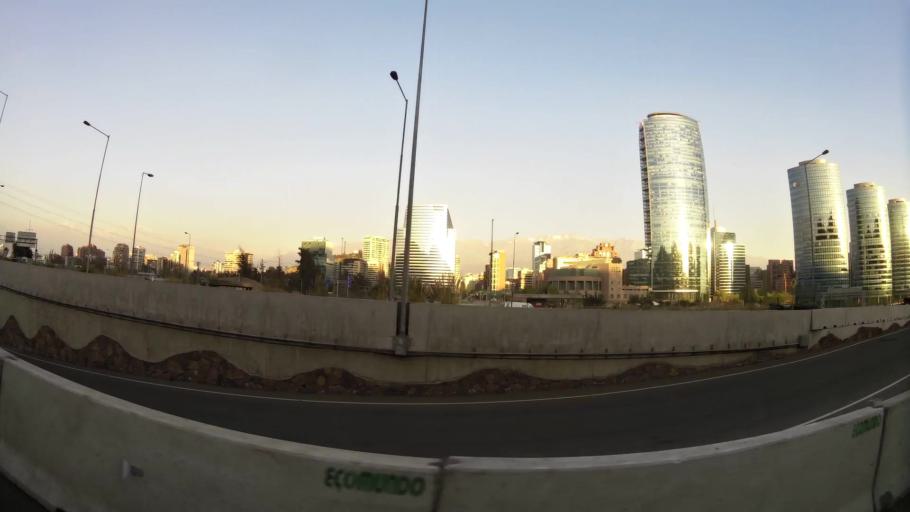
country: CL
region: Santiago Metropolitan
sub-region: Provincia de Santiago
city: Villa Presidente Frei, Nunoa, Santiago, Chile
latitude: -33.4105
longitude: -70.6075
